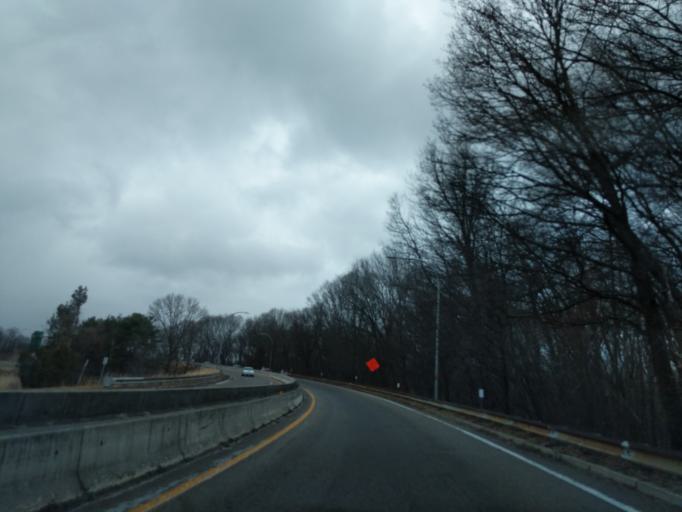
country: US
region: Rhode Island
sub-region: Kent County
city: Warwick
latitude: 41.7308
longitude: -71.4586
